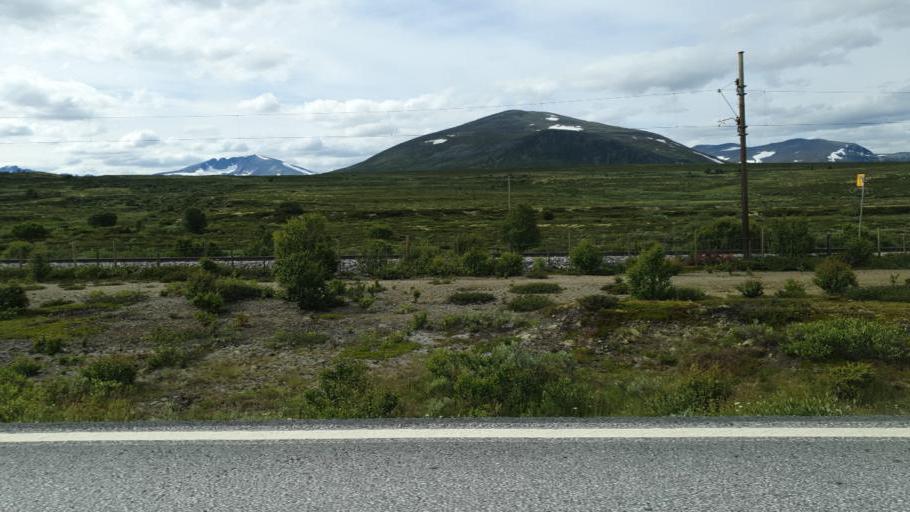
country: NO
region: Sor-Trondelag
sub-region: Oppdal
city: Oppdal
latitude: 62.2577
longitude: 9.5531
